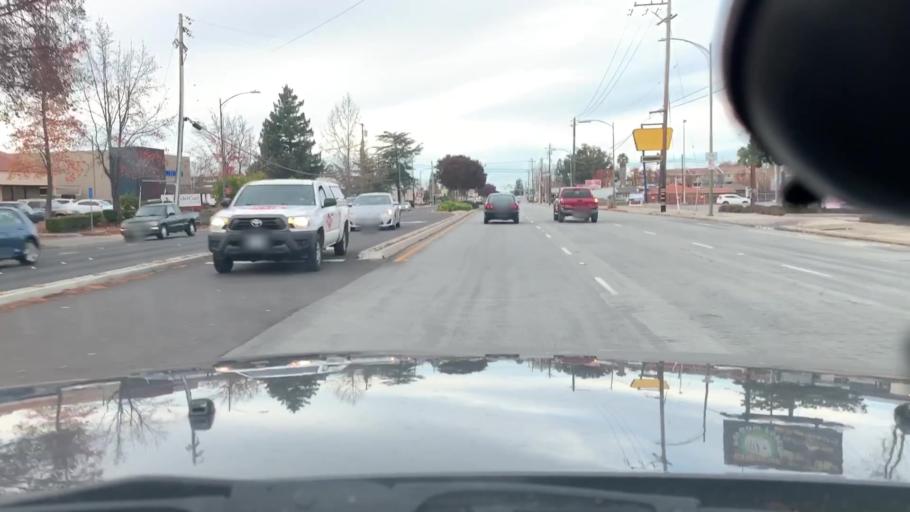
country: US
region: California
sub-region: Santa Clara County
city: Cupertino
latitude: 37.2961
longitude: -122.0322
